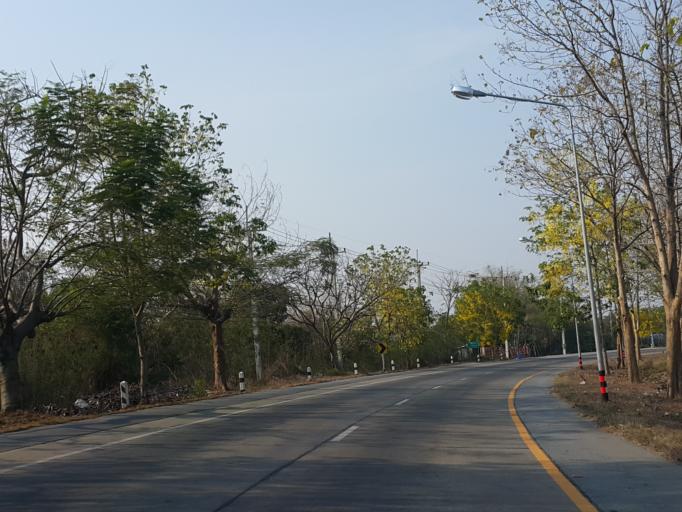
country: TH
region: Suphan Buri
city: Sam Chuk
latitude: 14.7849
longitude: 100.0880
